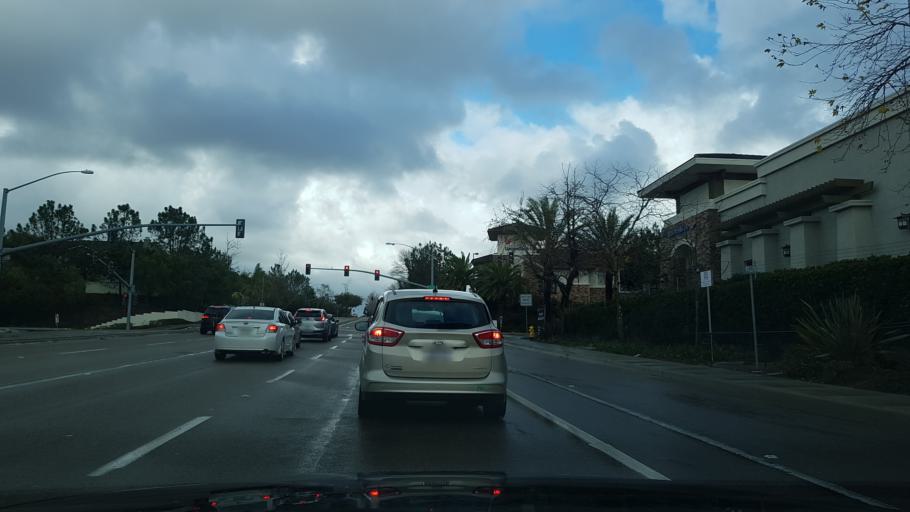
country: US
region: California
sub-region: San Diego County
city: Del Mar
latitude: 32.9212
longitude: -117.2169
